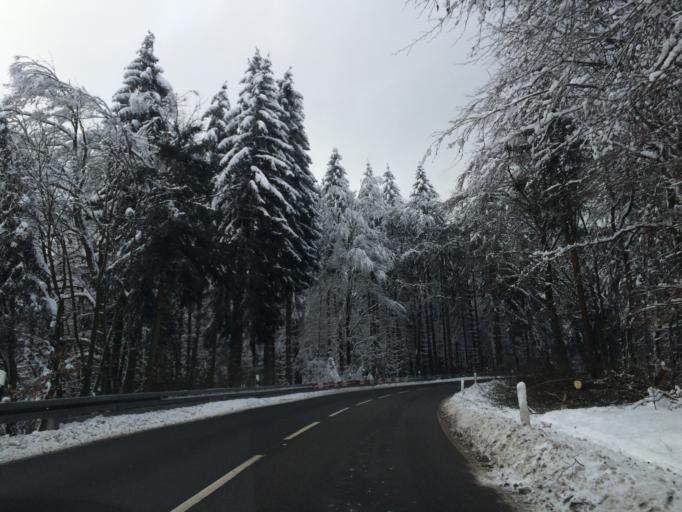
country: DE
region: Hesse
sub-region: Regierungsbezirk Darmstadt
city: Schmitten
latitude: 50.2311
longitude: 8.4358
